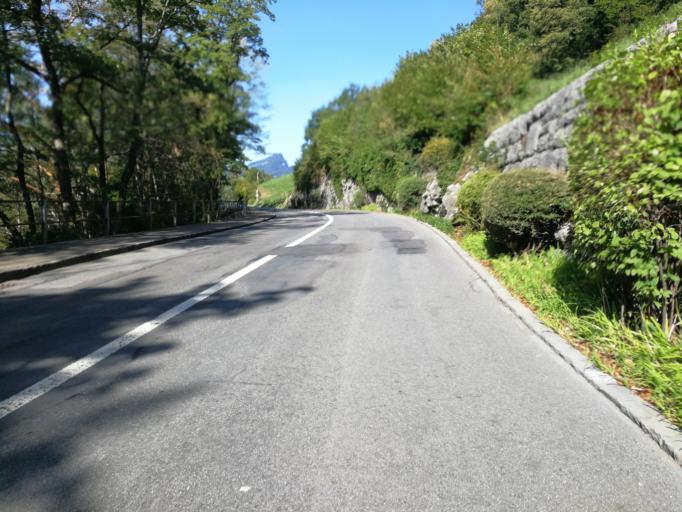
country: CH
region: Lucerne
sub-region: Lucerne-Land District
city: Vitznau
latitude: 46.9907
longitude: 8.4952
